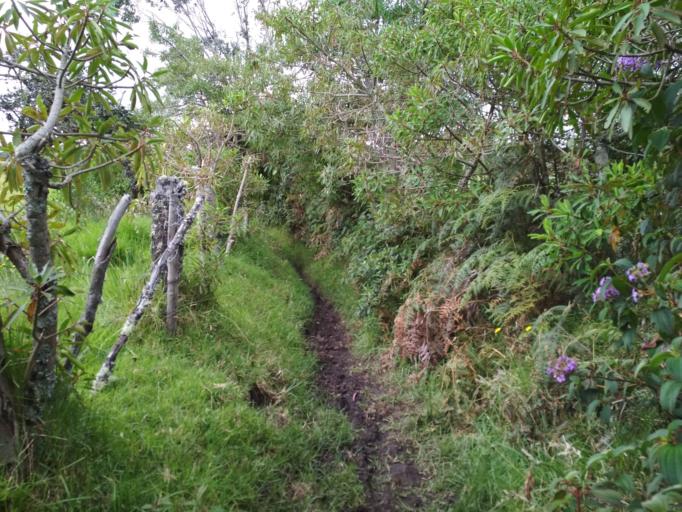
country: CO
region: Cauca
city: Totoro
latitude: 2.5194
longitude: -76.3910
